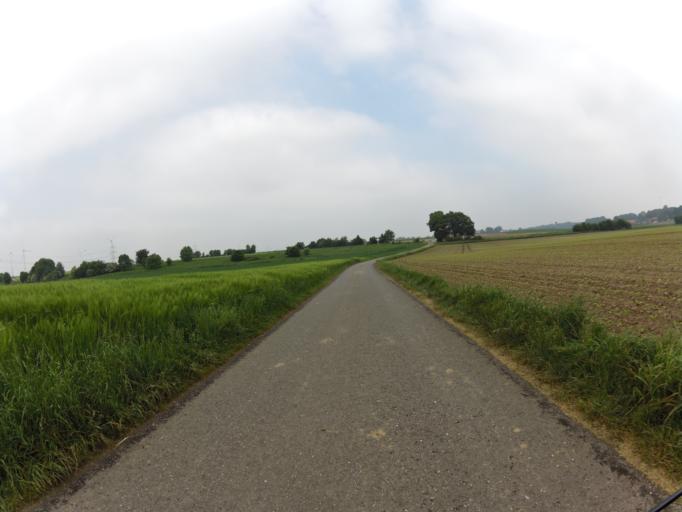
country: DE
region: North Rhine-Westphalia
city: Geilenkirchen
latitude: 51.0093
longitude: 6.1299
